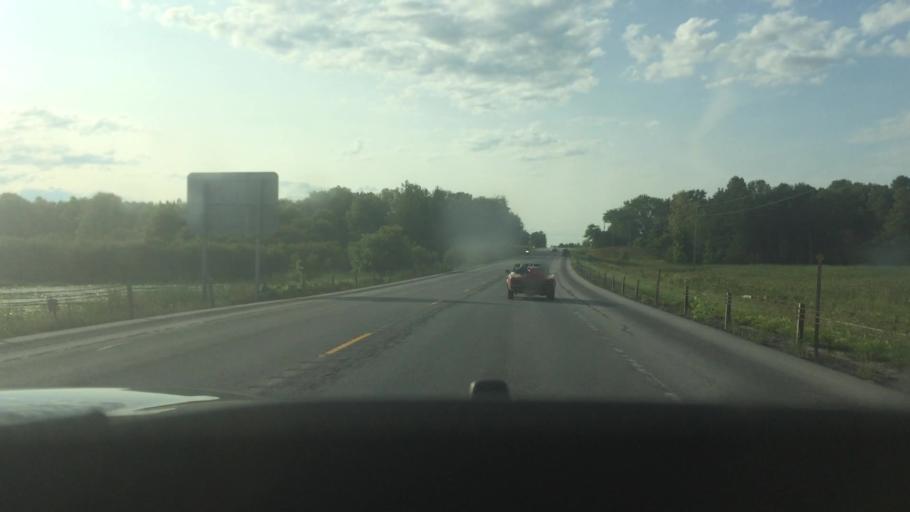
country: US
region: New York
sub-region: St. Lawrence County
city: Canton
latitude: 44.6226
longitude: -75.2319
